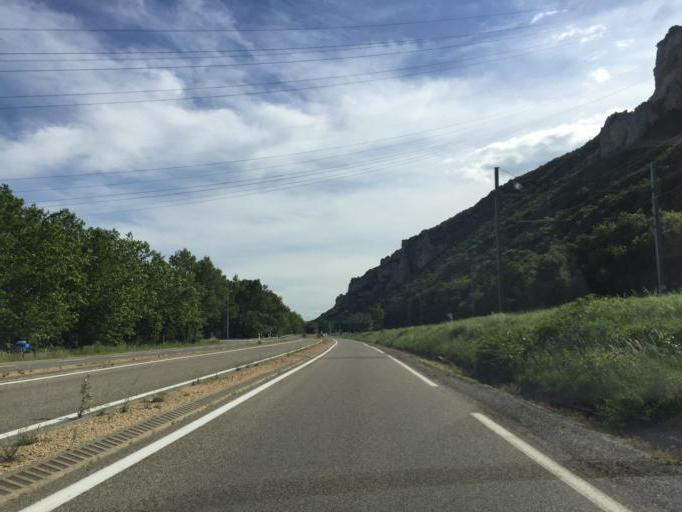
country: FR
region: Rhone-Alpes
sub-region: Departement de l'Ardeche
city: Cruas
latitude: 44.6359
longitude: 4.7464
